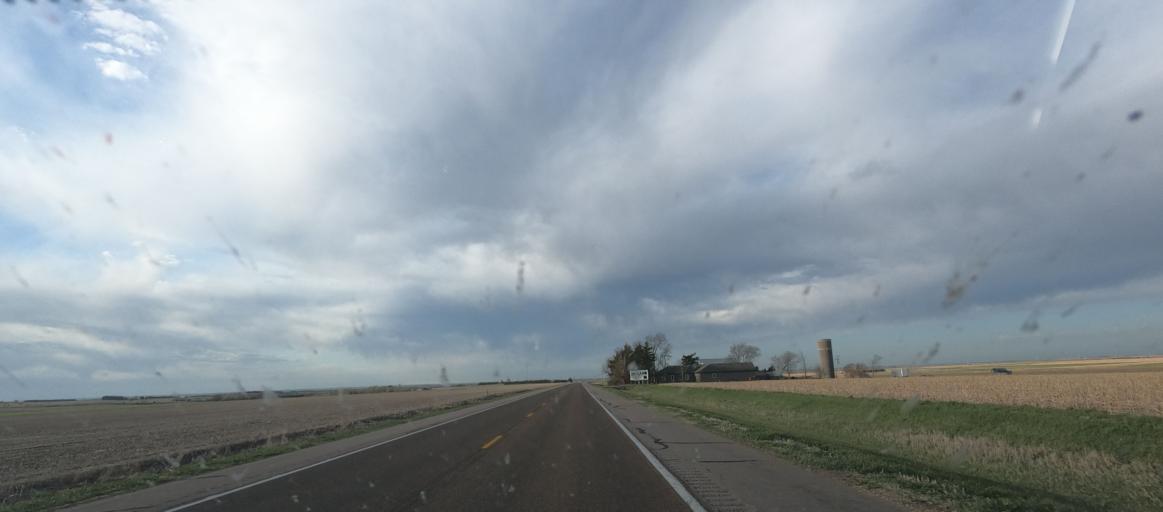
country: US
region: Nebraska
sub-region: Harlan County
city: Alma
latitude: 40.1444
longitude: -99.3674
